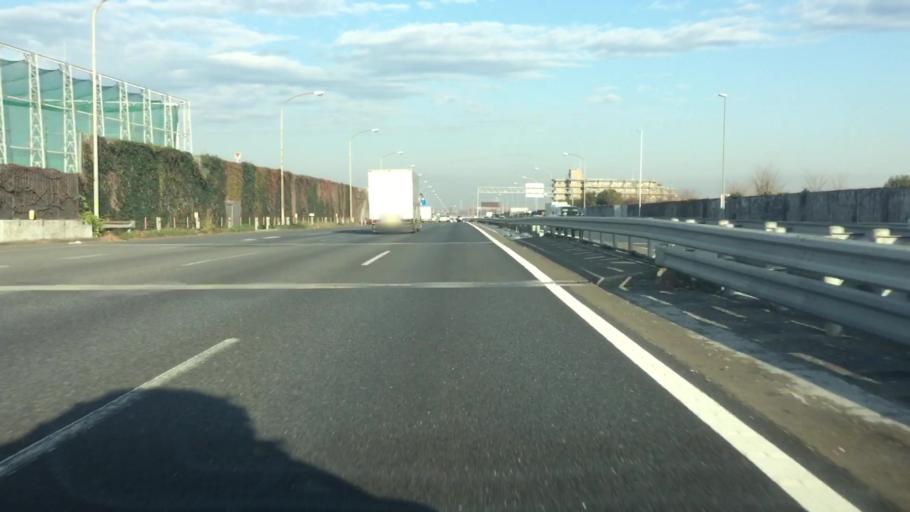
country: JP
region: Saitama
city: Kawagoe
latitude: 35.8952
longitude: 139.4579
